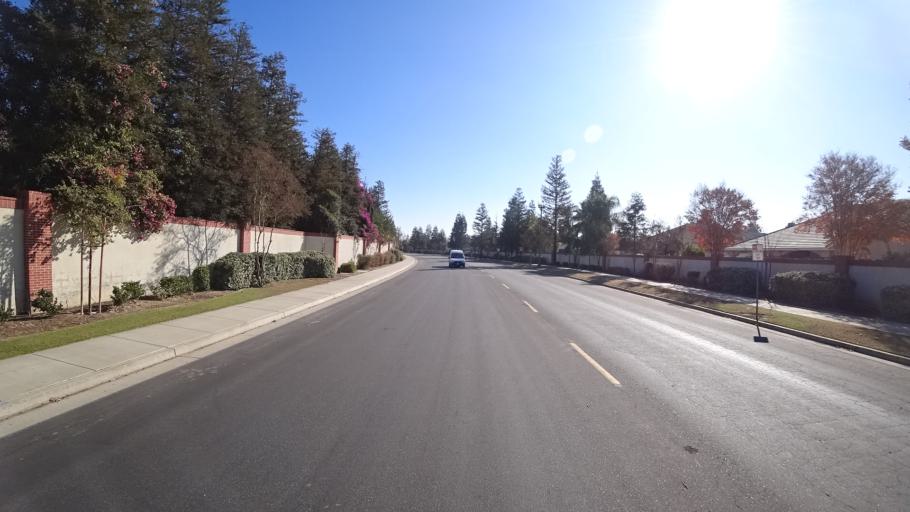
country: US
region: California
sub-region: Kern County
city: Greenacres
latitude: 35.3307
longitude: -119.1245
